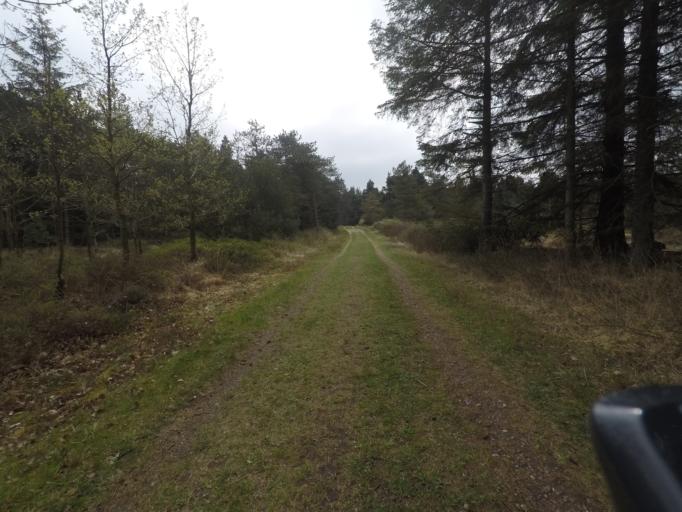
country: DE
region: Schleswig-Holstein
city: List
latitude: 55.1027
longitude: 8.5239
